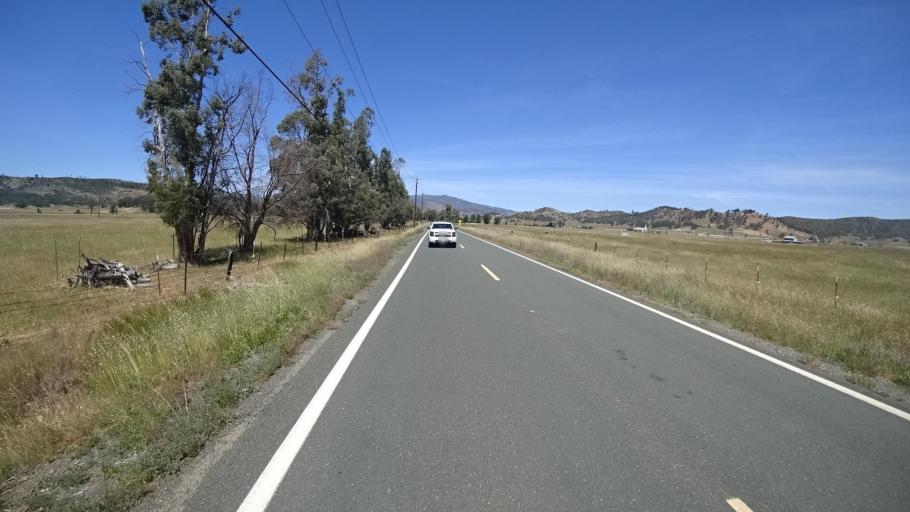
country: US
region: California
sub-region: Lake County
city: Middletown
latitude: 38.7442
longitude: -122.5754
